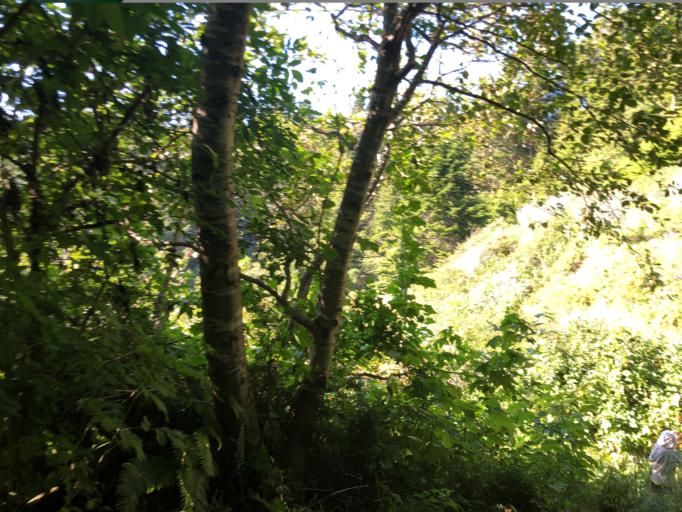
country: US
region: California
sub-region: Humboldt County
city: Westhaven-Moonstone
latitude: 41.0611
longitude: -124.1474
